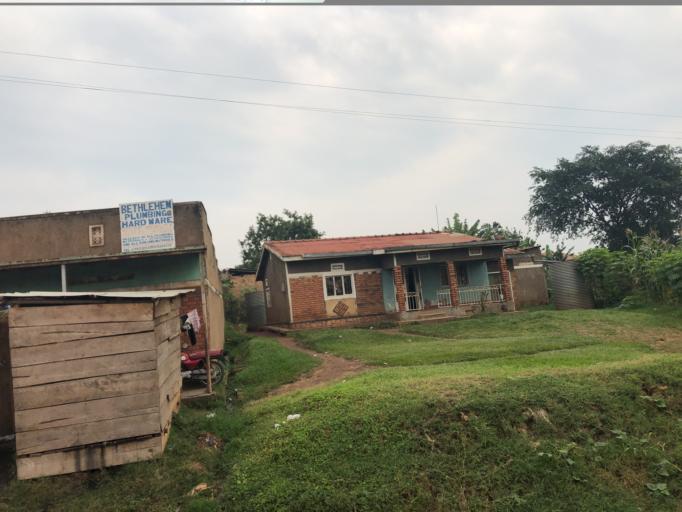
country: UG
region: Central Region
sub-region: Mukono District
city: Mukono
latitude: 0.3464
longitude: 32.7639
